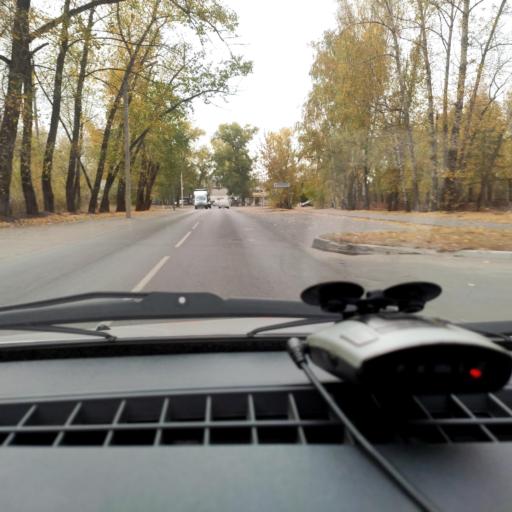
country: RU
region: Voronezj
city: Podgornoye
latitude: 51.7410
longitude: 39.1738
